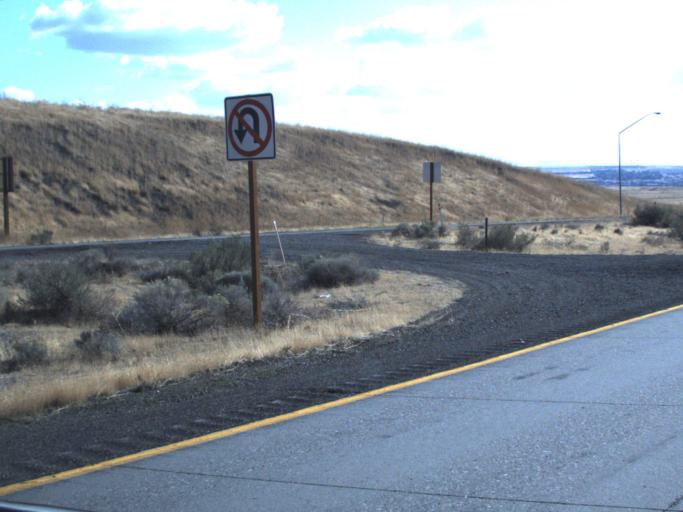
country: US
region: Oregon
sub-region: Umatilla County
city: Umatilla
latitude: 45.9683
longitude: -119.3411
